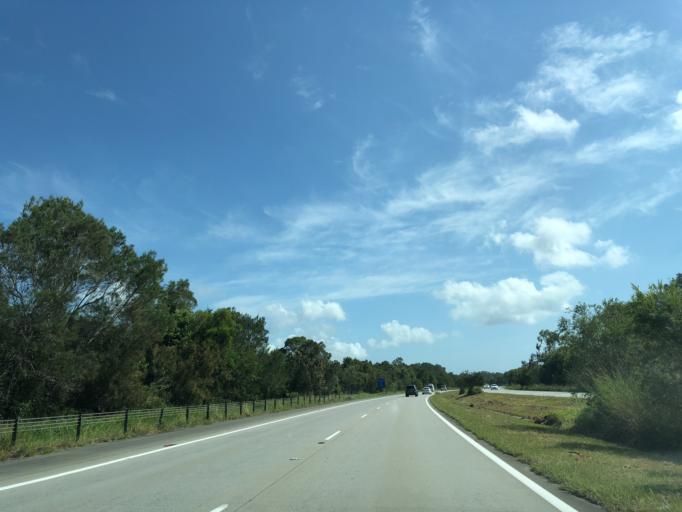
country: AU
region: New South Wales
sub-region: Byron Shire
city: Brunswick Heads
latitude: -28.5691
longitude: 153.5407
